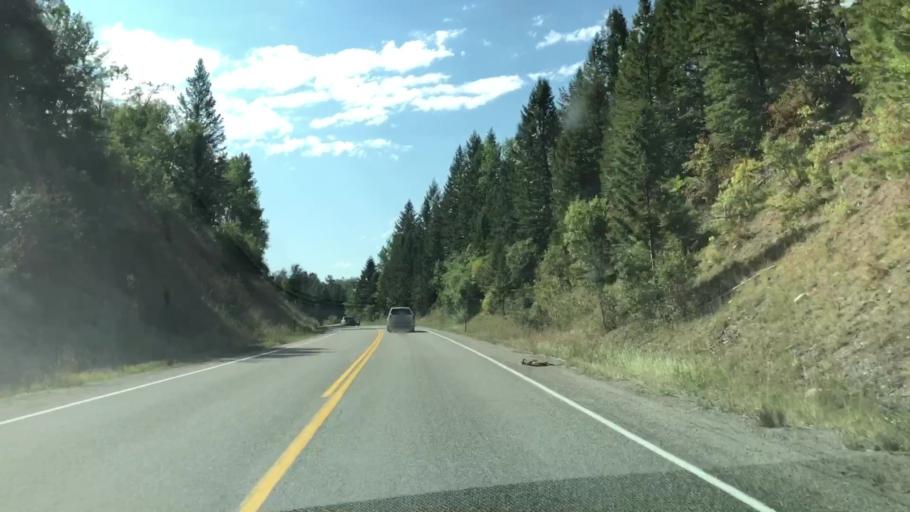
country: US
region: Idaho
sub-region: Teton County
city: Victor
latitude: 43.2987
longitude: -111.1291
